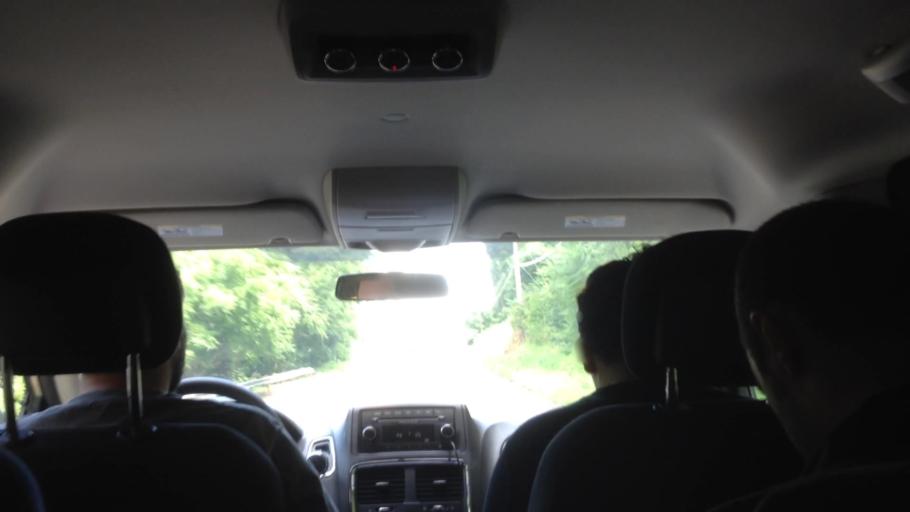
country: US
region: New York
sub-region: Dutchess County
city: Red Hook
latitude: 42.0174
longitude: -73.8521
